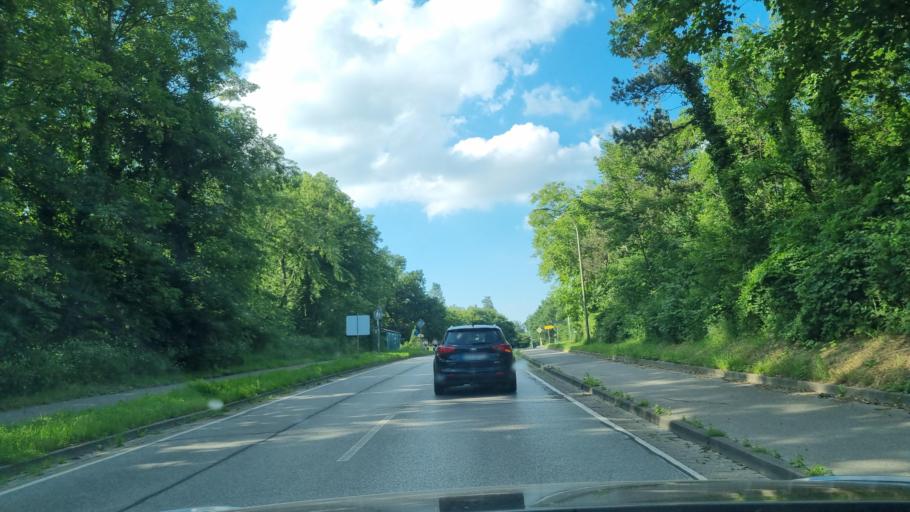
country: DE
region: North Rhine-Westphalia
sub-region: Regierungsbezirk Dusseldorf
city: Goch
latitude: 51.7089
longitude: 6.1284
